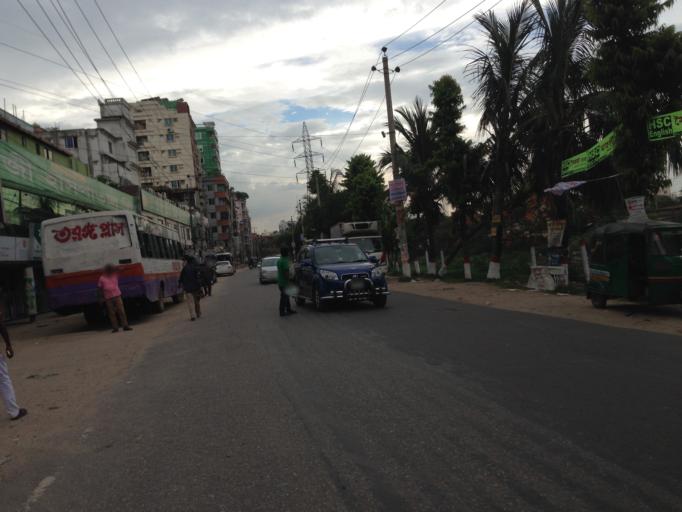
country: BD
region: Dhaka
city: Paltan
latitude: 23.7626
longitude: 90.4367
